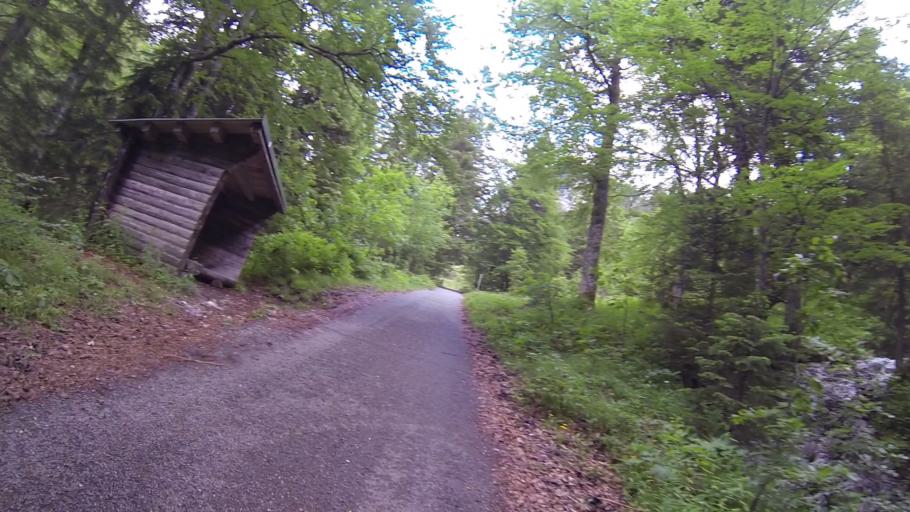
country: DE
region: Bavaria
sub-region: Swabia
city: Schwangau
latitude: 47.5329
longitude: 10.7948
